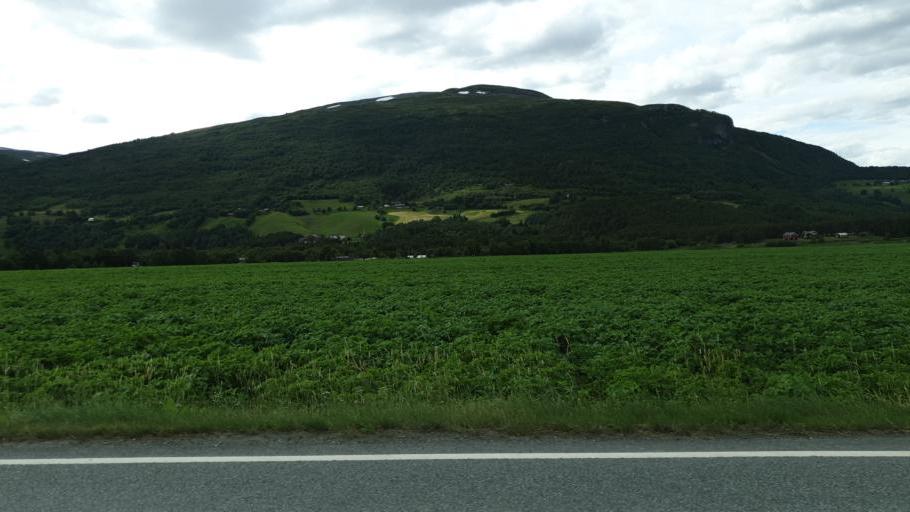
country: NO
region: Sor-Trondelag
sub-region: Oppdal
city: Oppdal
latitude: 62.5379
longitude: 9.6267
